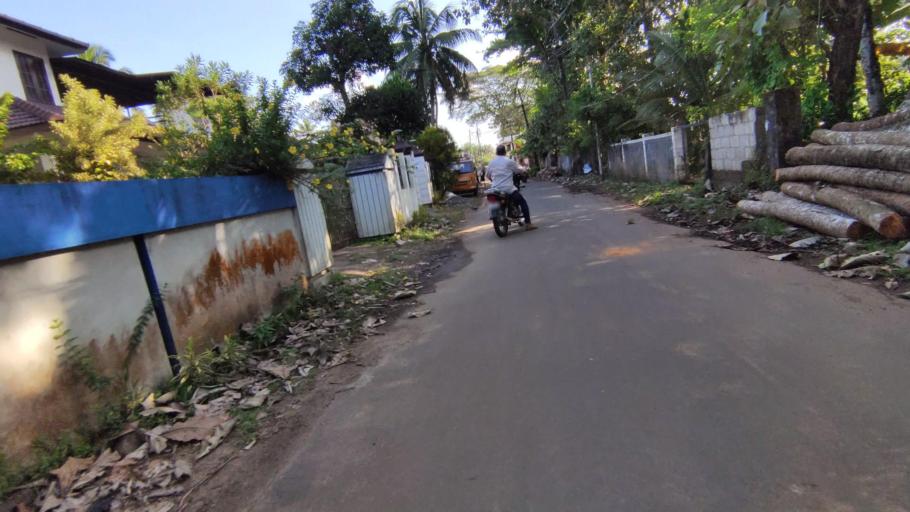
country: IN
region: Kerala
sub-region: Kottayam
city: Kottayam
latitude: 9.5976
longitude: 76.5038
